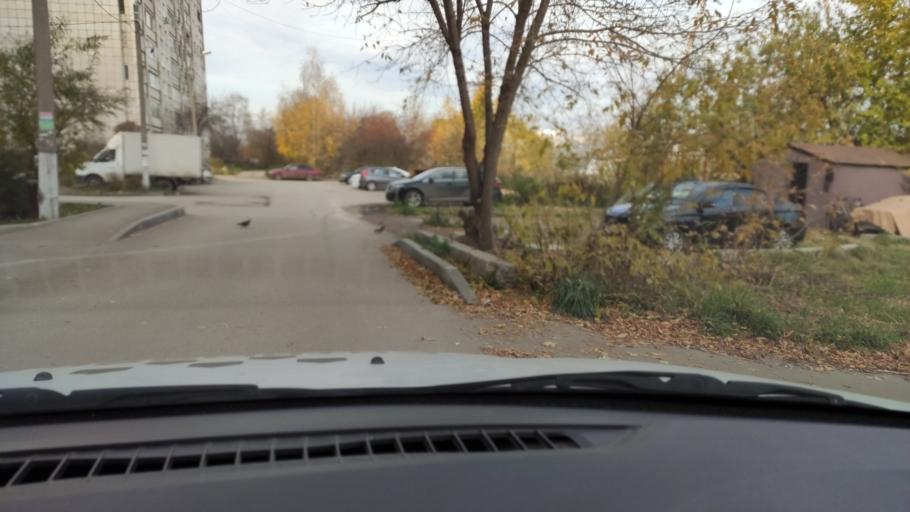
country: RU
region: Perm
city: Perm
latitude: 57.9797
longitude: 56.2801
